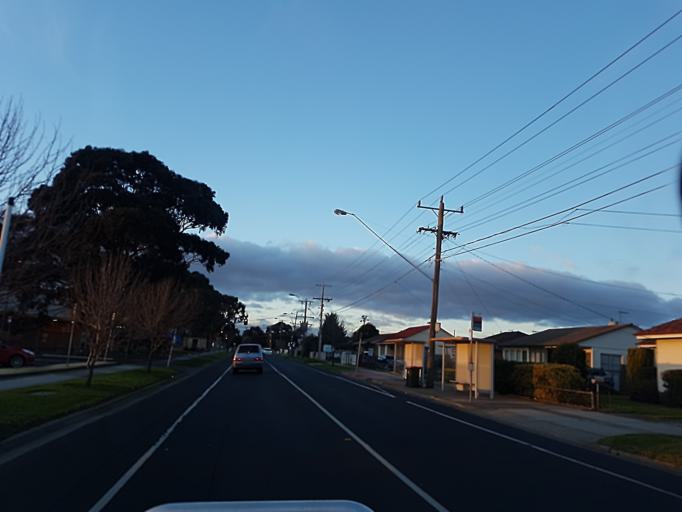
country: AU
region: Victoria
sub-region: Hume
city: Broadmeadows
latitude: -37.6743
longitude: 144.9304
